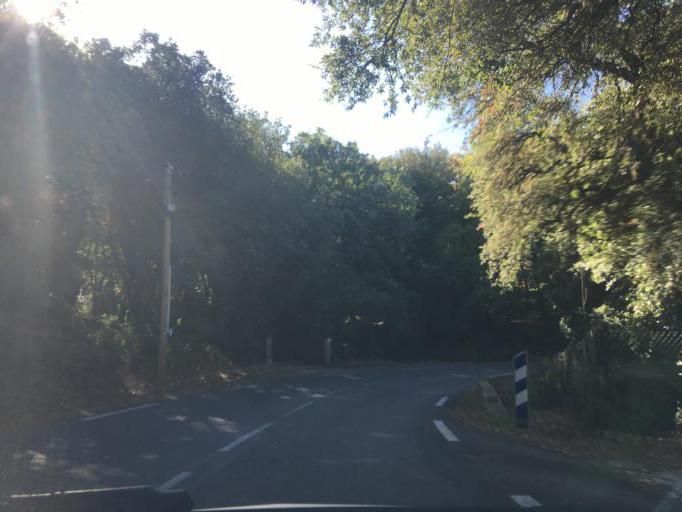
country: FR
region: Provence-Alpes-Cote d'Azur
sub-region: Departement du Var
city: La Garde-Freinet
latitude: 43.3217
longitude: 6.4742
